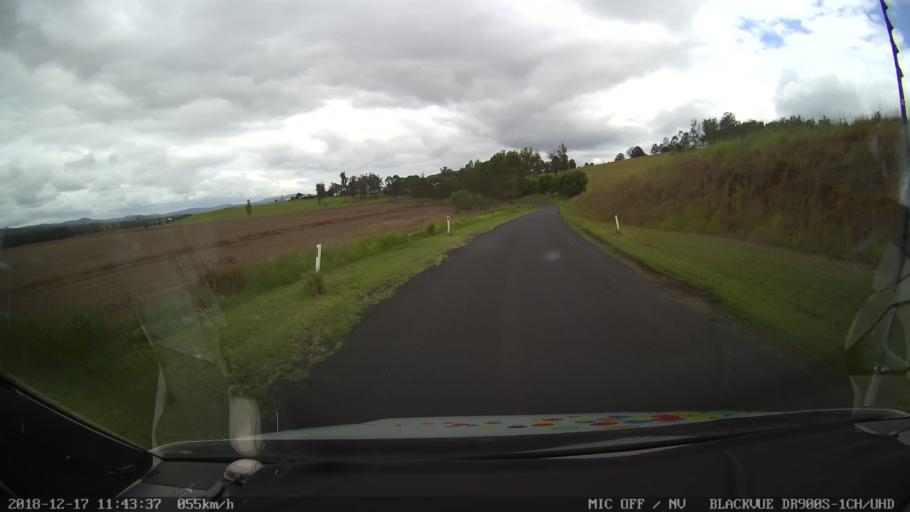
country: AU
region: New South Wales
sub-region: Kyogle
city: Kyogle
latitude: -28.6585
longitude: 152.5932
